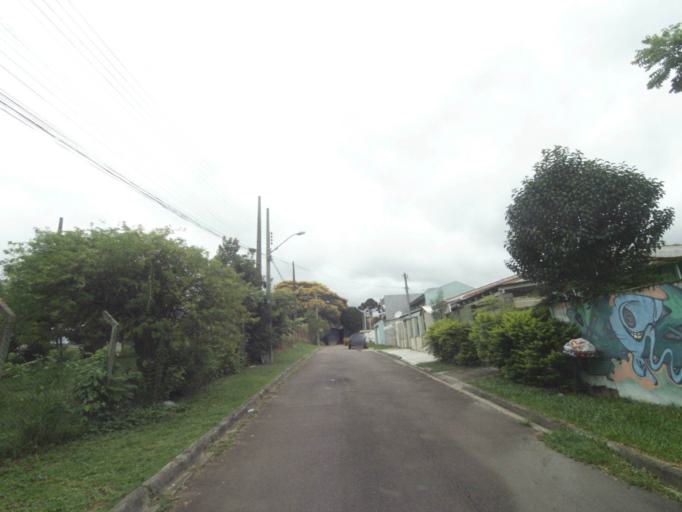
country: BR
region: Parana
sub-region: Curitiba
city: Curitiba
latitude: -25.4856
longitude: -49.2995
